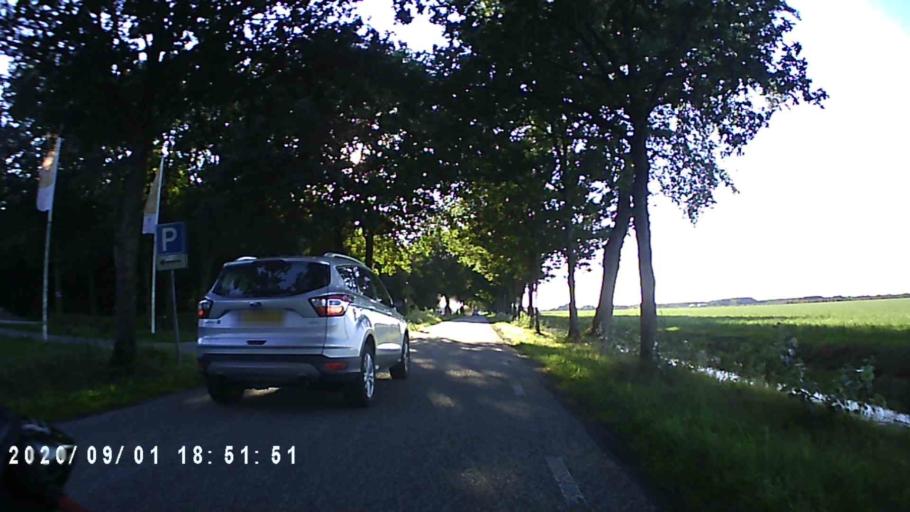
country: NL
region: Groningen
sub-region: Gemeente Veendam
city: Veendam
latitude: 53.1369
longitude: 6.8475
